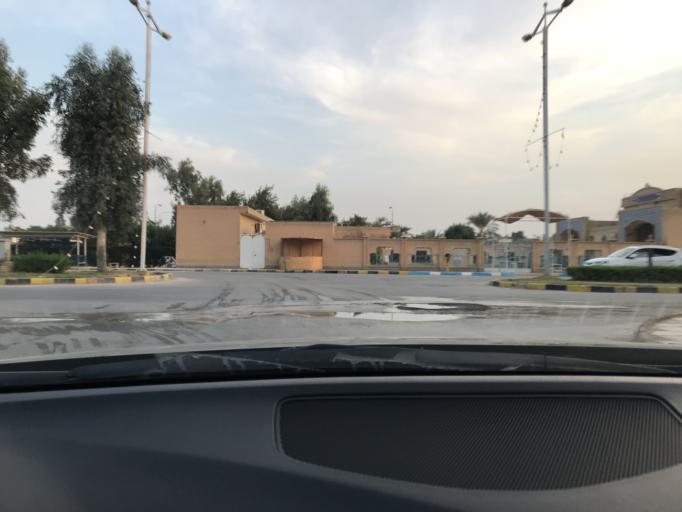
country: IR
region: Khuzestan
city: Ahvaz
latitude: 31.3299
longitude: 48.7362
